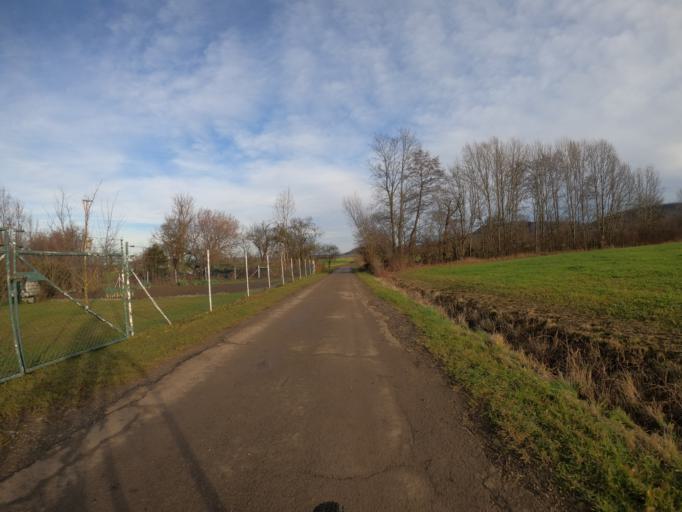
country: DE
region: Baden-Wuerttemberg
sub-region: Regierungsbezirk Stuttgart
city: Durnau
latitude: 48.6486
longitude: 9.6316
